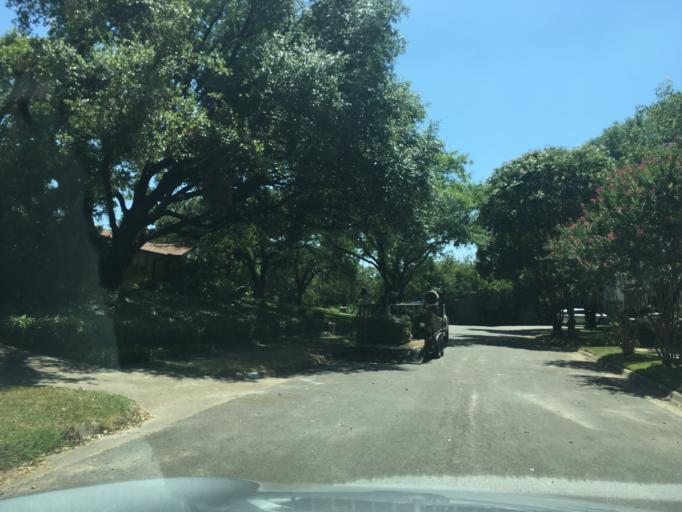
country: US
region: Texas
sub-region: Dallas County
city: Highland Park
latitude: 32.8645
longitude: -96.7265
